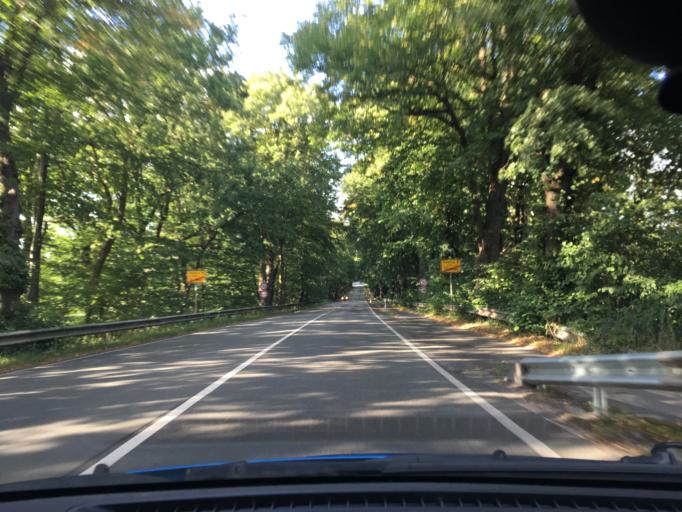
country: DE
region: Lower Saxony
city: Seevetal
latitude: 53.4069
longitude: 9.9256
